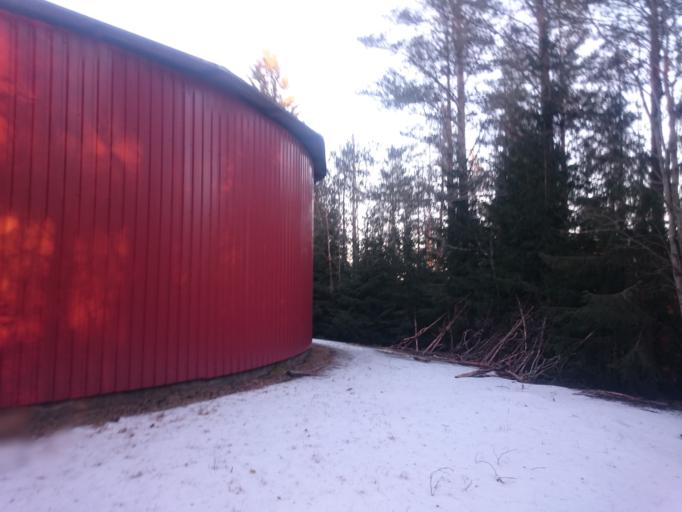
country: SE
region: Vaesternorrland
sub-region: OErnskoeldsviks Kommun
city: Bredbyn
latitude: 63.3025
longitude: 18.2588
